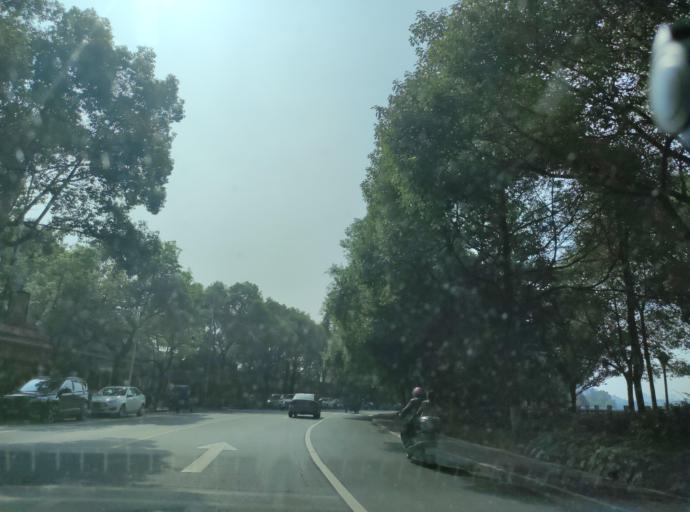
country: CN
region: Jiangxi Sheng
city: Pingxiang
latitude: 27.6417
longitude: 113.8561
